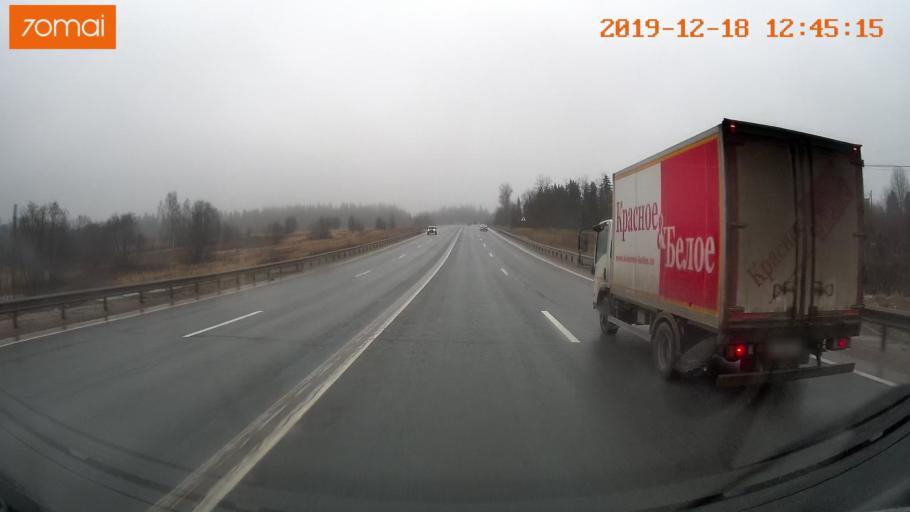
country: RU
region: Moskovskaya
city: Klin
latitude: 56.2291
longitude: 36.6570
